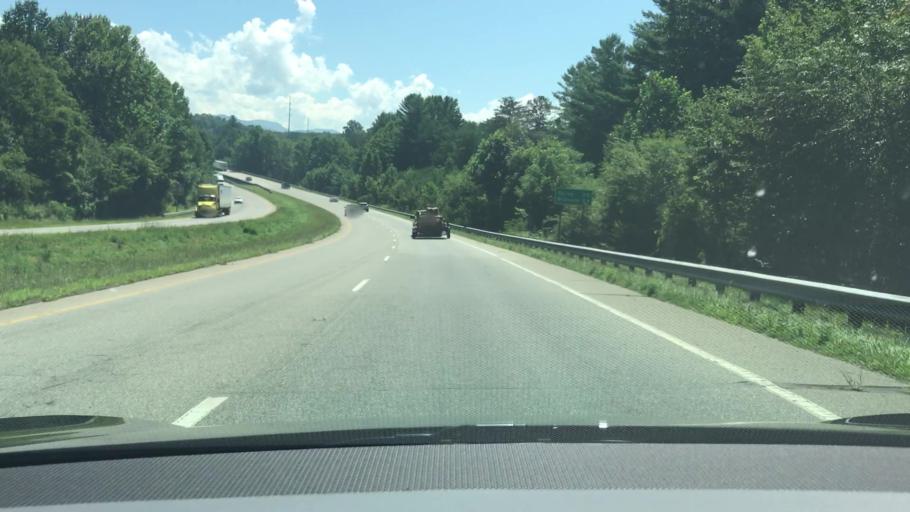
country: US
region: North Carolina
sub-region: Macon County
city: Franklin
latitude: 35.1641
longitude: -83.3796
